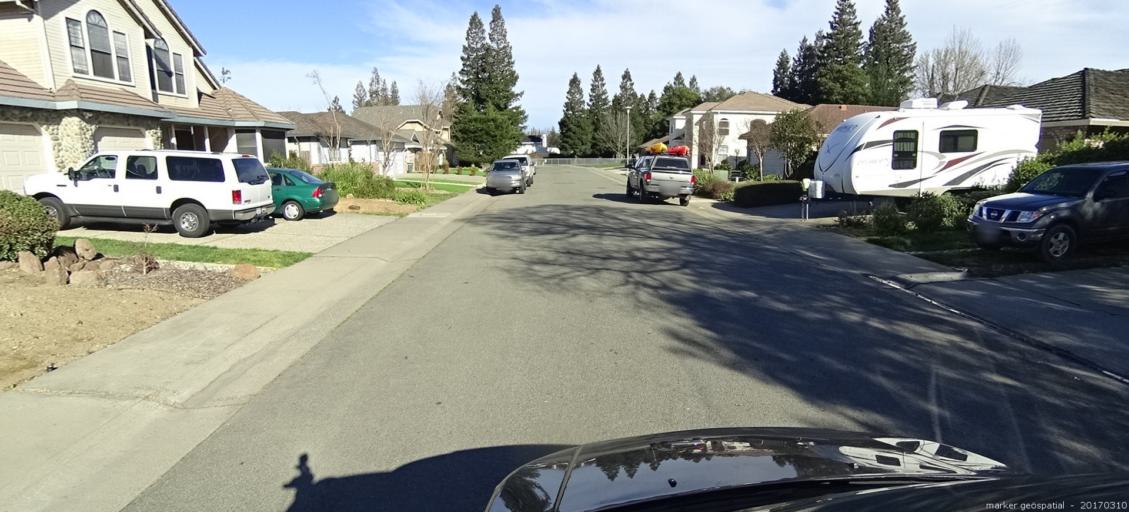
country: US
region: California
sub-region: Sacramento County
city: Parkway
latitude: 38.4921
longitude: -121.5362
